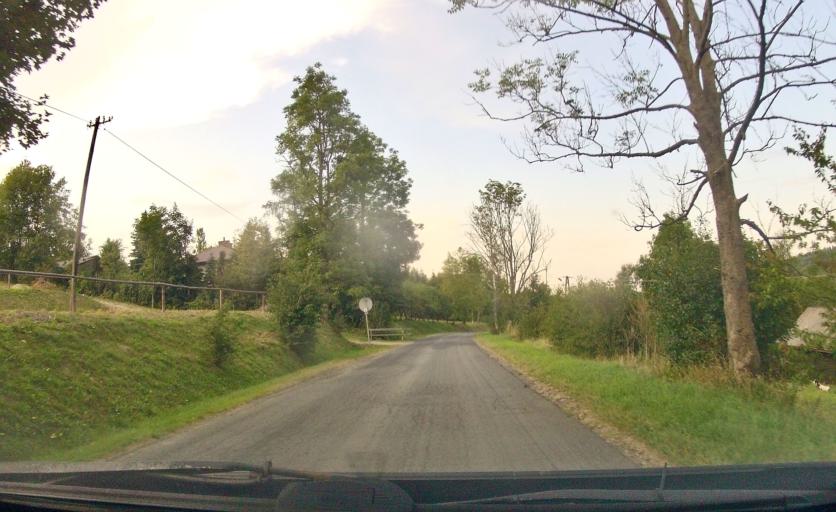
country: PL
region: Subcarpathian Voivodeship
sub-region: Powiat krosnienski
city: Dukla
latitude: 49.5331
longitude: 21.6153
